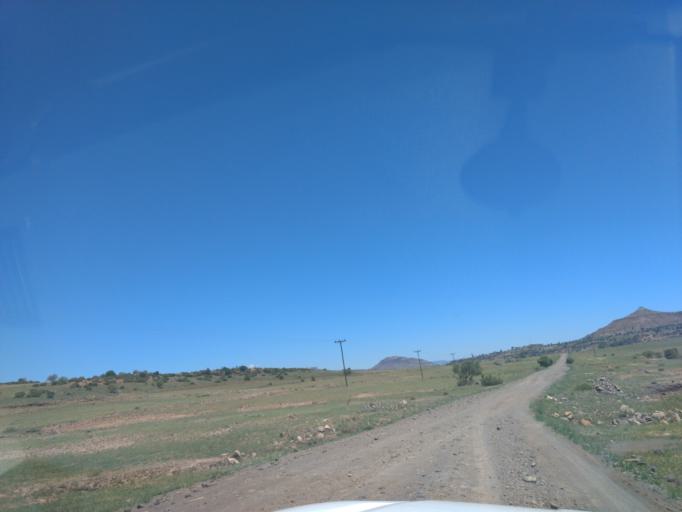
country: LS
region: Maseru
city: Maseru
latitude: -29.4700
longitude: 27.3756
